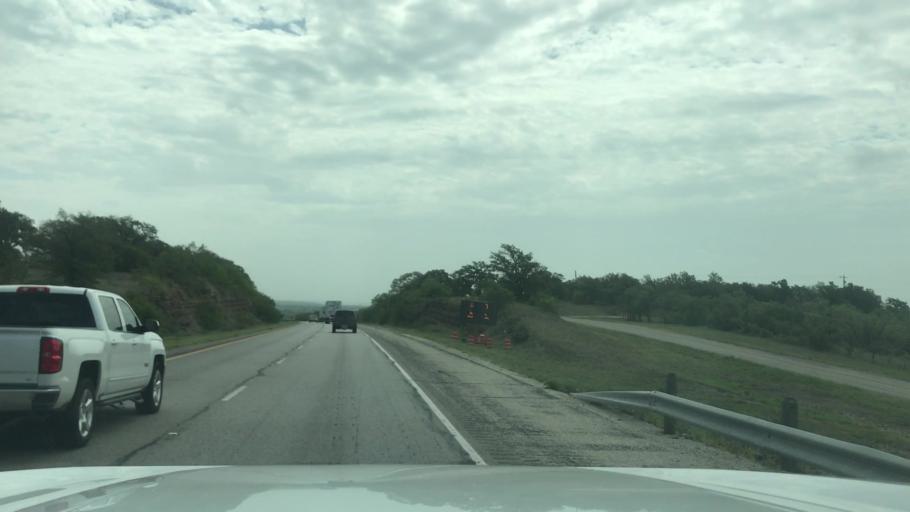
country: US
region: Texas
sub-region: Callahan County
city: Baird
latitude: 32.4044
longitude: -99.4331
